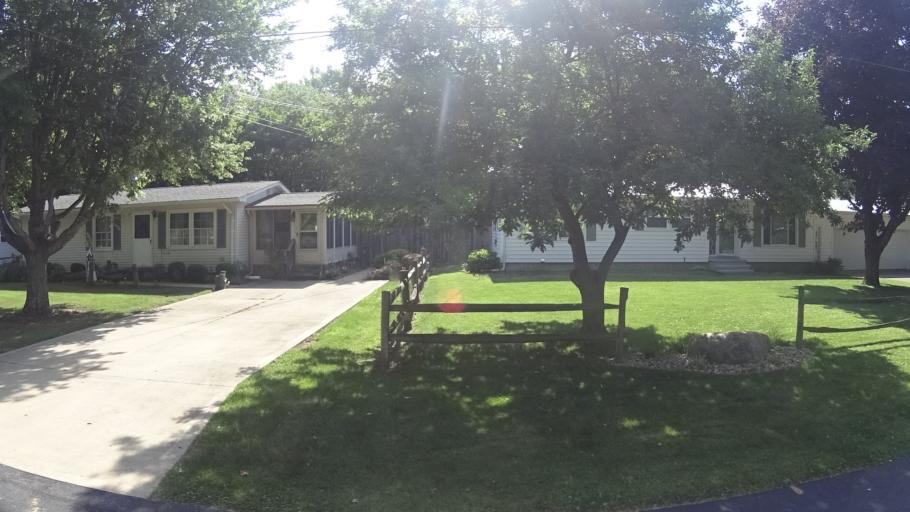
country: US
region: Ohio
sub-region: Erie County
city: Huron
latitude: 41.3805
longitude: -82.5056
